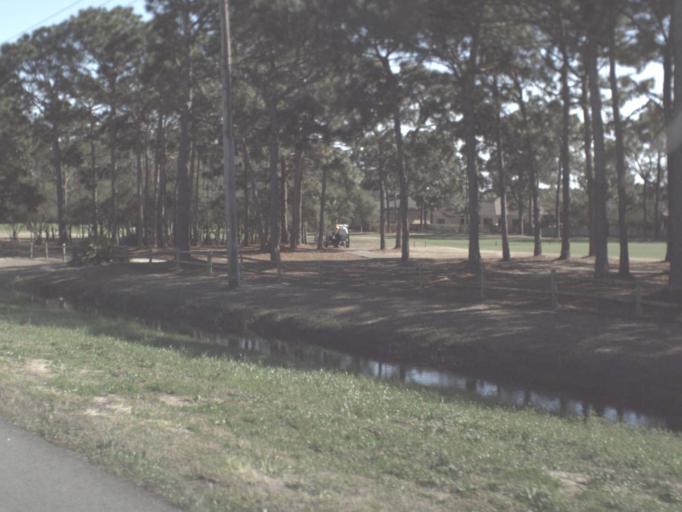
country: US
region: Florida
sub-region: Bay County
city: Panama City Beach
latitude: 30.1918
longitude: -85.7972
